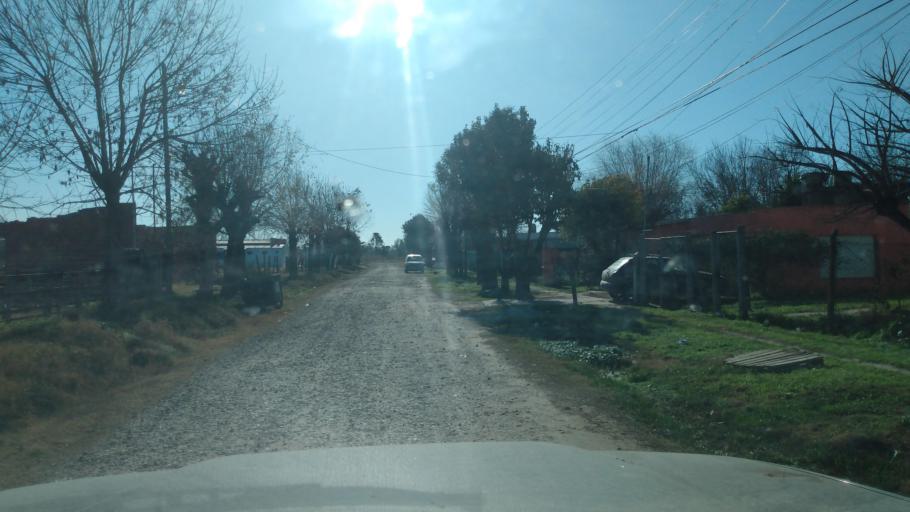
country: AR
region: Buenos Aires
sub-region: Partido de Lujan
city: Lujan
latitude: -34.5664
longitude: -59.0835
